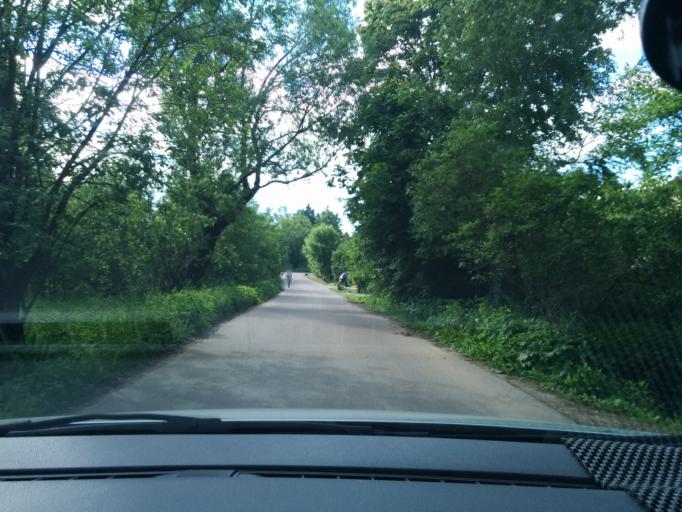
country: RU
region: Moskovskaya
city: Lugovaya
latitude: 56.0533
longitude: 37.4799
